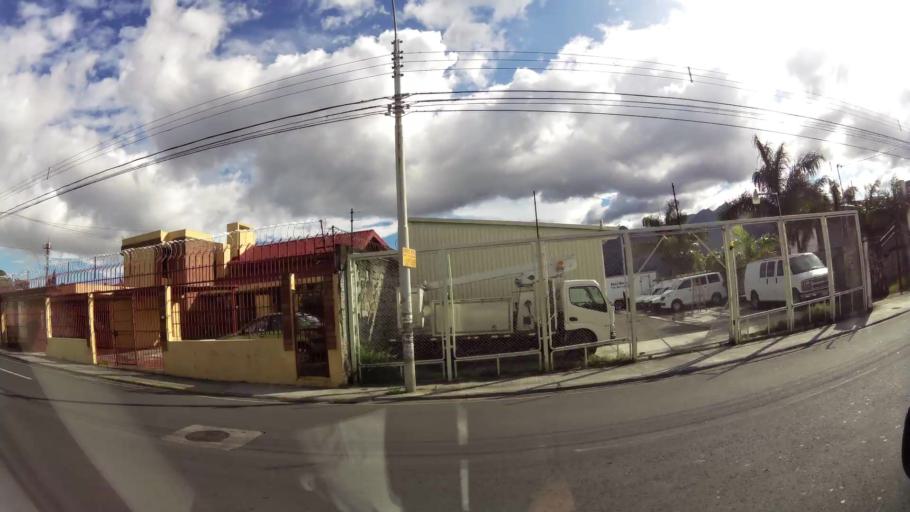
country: CR
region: San Jose
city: San Rafael
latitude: 9.9336
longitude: -84.1130
